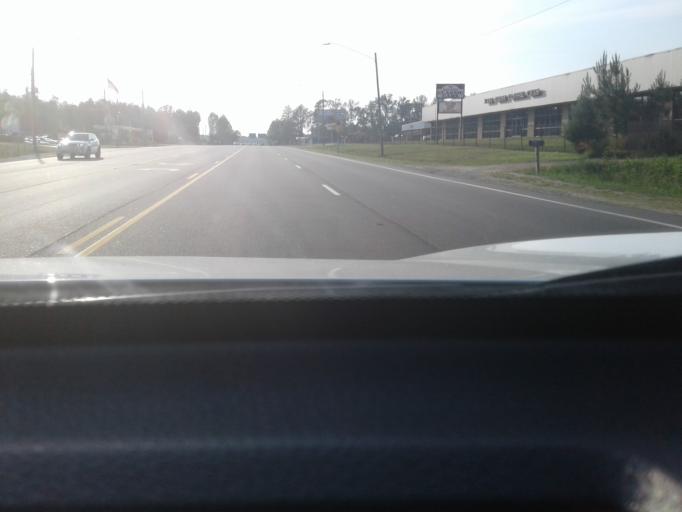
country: US
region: North Carolina
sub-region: Harnett County
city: Lillington
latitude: 35.4150
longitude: -78.7972
